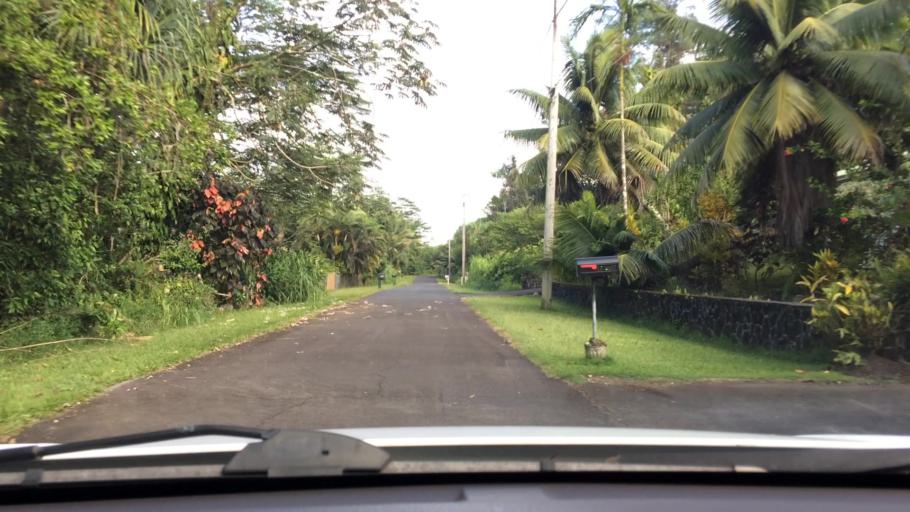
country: US
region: Hawaii
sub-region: Hawaii County
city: Hawaiian Beaches
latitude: 19.5446
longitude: -154.8991
